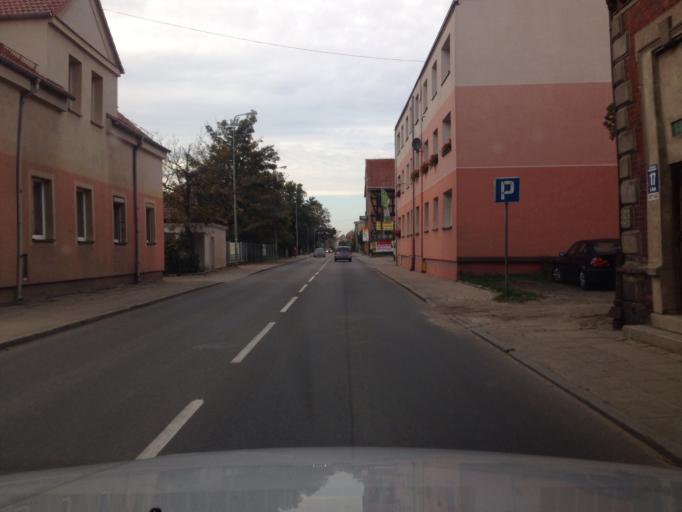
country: PL
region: Pomeranian Voivodeship
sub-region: Powiat leborski
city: Lebork
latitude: 54.5469
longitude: 17.7507
